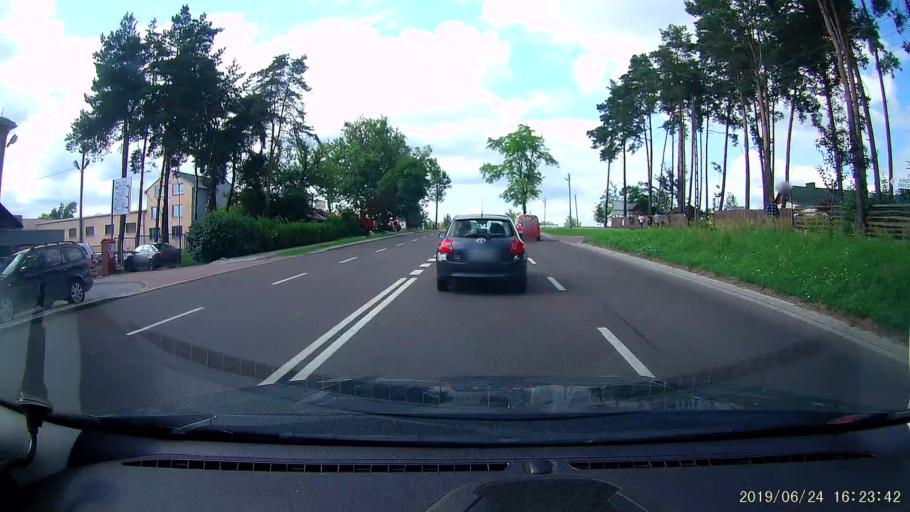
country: PL
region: Lublin Voivodeship
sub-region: Powiat tomaszowski
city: Tomaszow Lubelski
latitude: 50.4342
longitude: 23.4206
